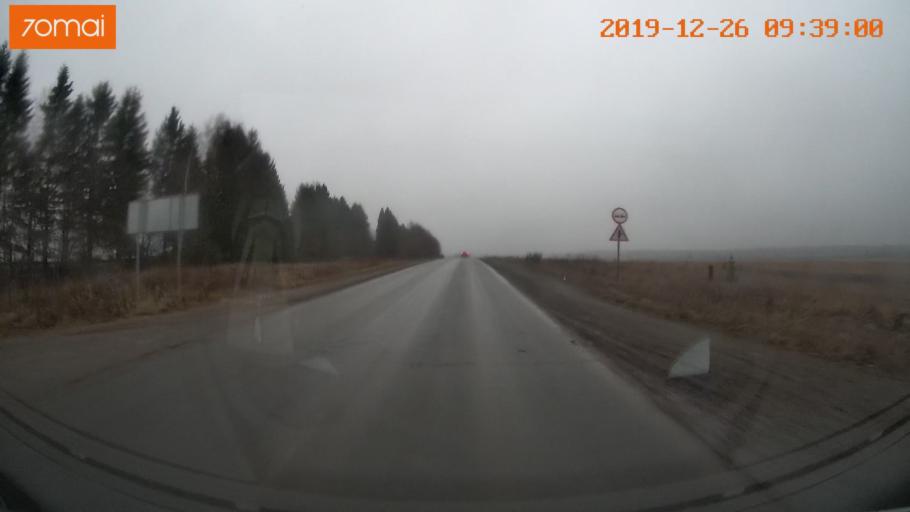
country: RU
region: Vologda
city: Vologda
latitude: 59.1500
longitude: 40.0327
